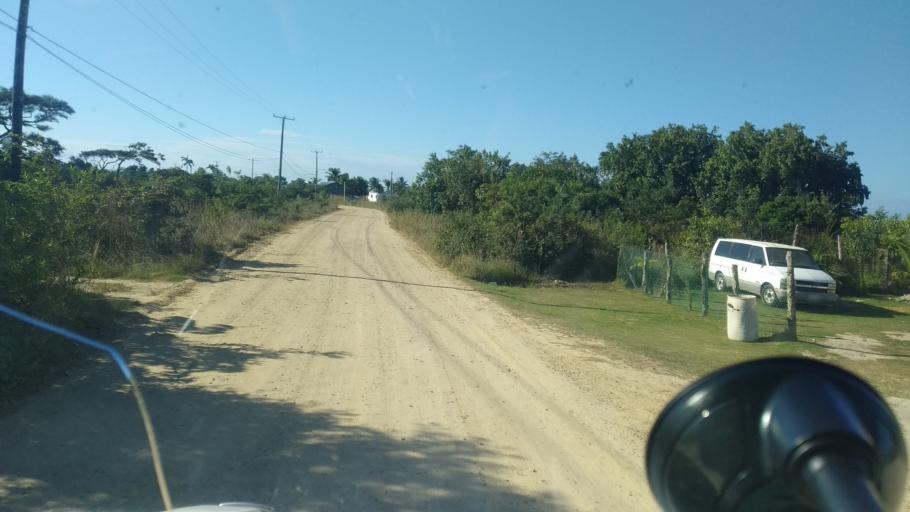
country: BZ
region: Belize
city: Belize City
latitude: 17.5615
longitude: -88.3269
